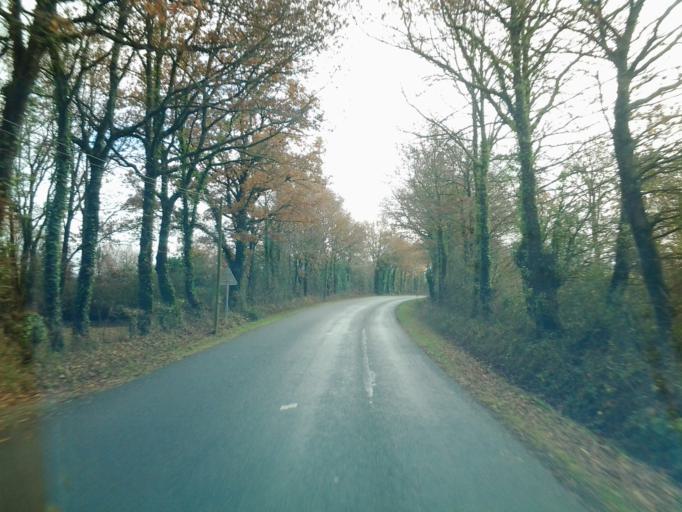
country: FR
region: Pays de la Loire
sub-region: Departement de la Vendee
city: Saint-Florent-des-Bois
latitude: 46.6342
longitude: -1.3352
